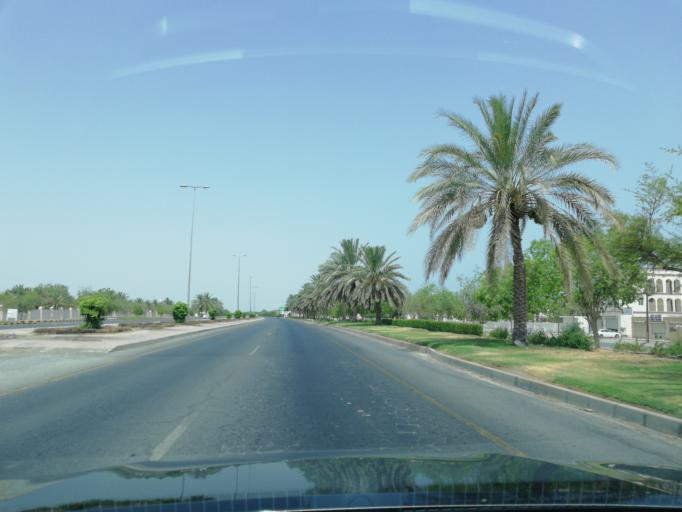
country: OM
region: Muhafazat Masqat
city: As Sib al Jadidah
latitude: 23.6934
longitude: 58.0666
